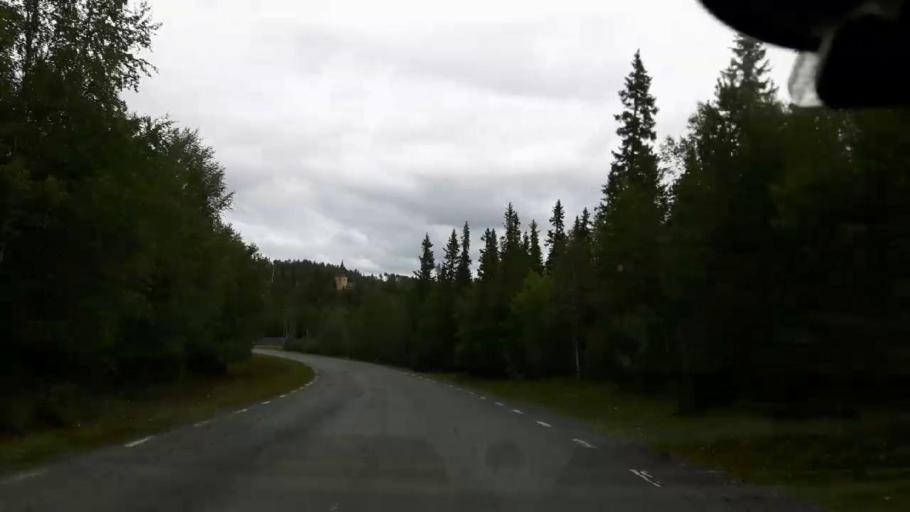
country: SE
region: Jaemtland
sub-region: Krokoms Kommun
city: Valla
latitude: 63.6444
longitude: 13.8269
